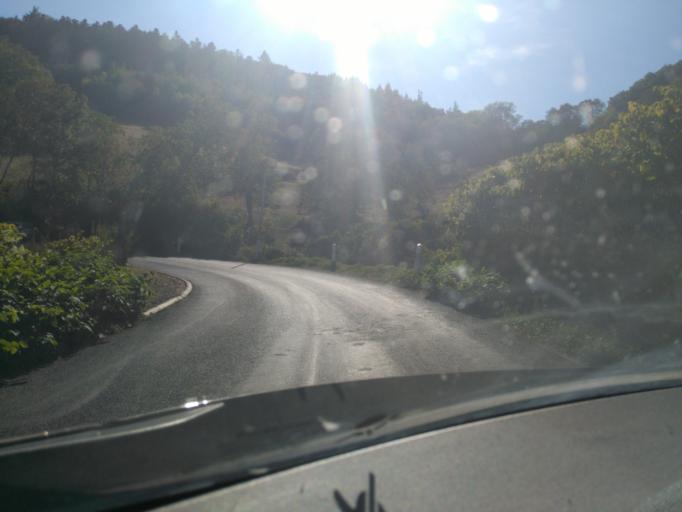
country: FR
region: Rhone-Alpes
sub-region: Departement du Rhone
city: Tarare
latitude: 45.8809
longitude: 4.4255
